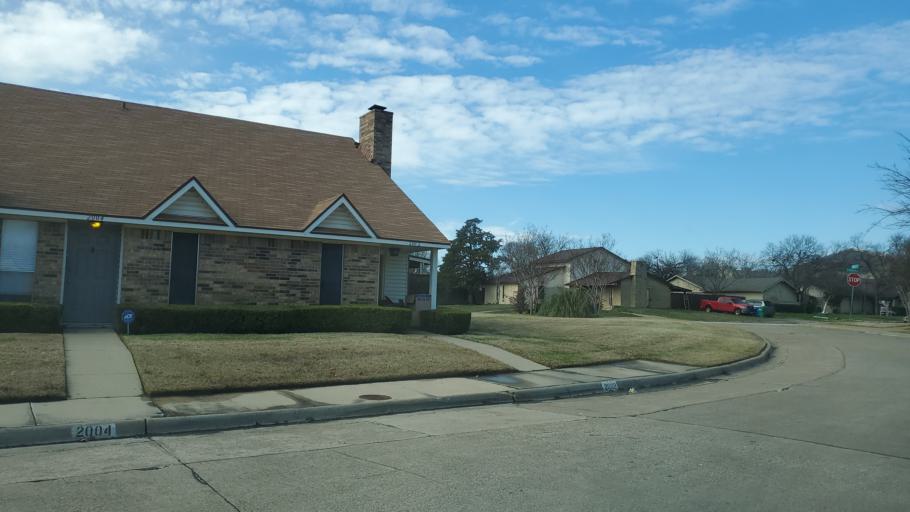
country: US
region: Texas
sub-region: Dallas County
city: Carrollton
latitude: 32.9786
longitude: -96.8880
